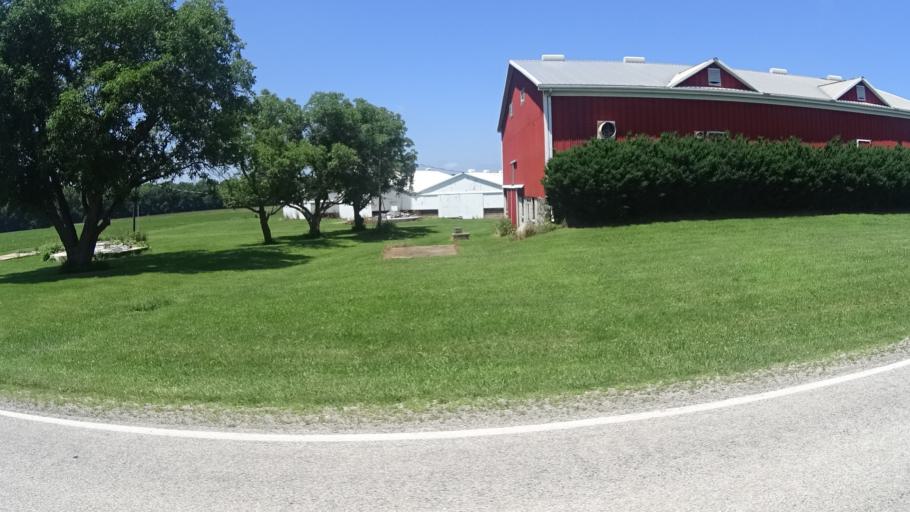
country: US
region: Ohio
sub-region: Lorain County
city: Vermilion
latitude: 41.3513
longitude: -82.4093
